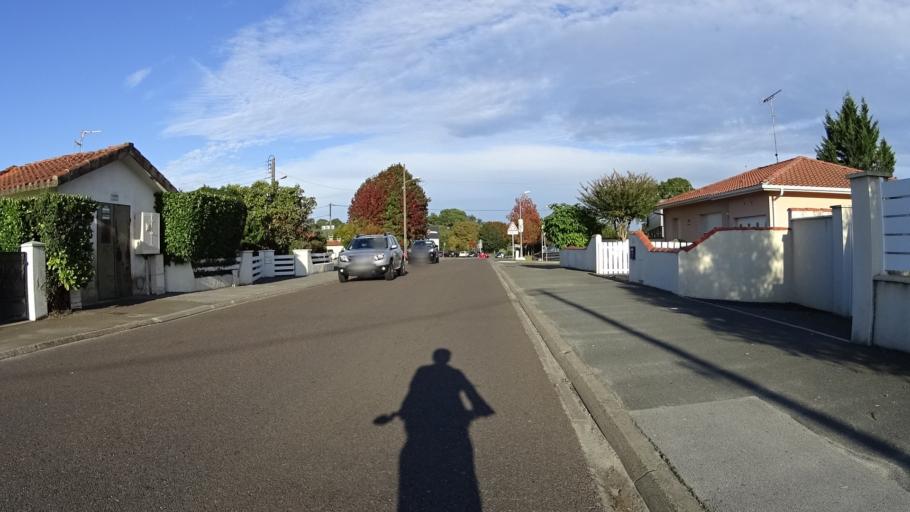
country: FR
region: Aquitaine
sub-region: Departement des Landes
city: Saint-Paul-les-Dax
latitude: 43.7360
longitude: -1.0527
